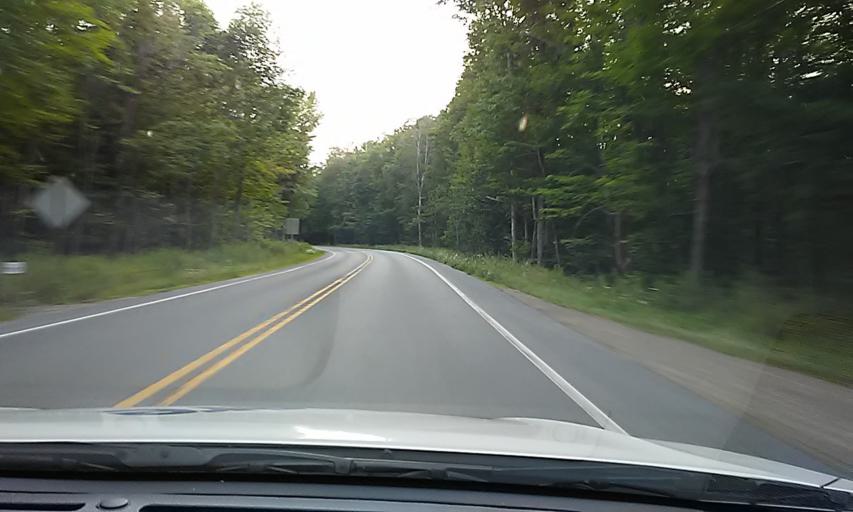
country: US
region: Pennsylvania
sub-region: McKean County
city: Kane
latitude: 41.6177
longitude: -78.8315
